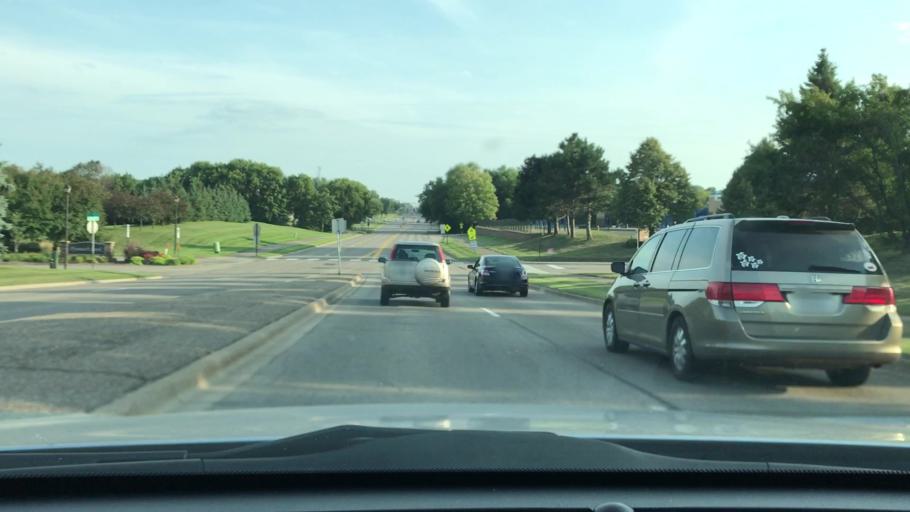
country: US
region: Minnesota
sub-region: Hennepin County
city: Plymouth
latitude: 45.0314
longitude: -93.4818
